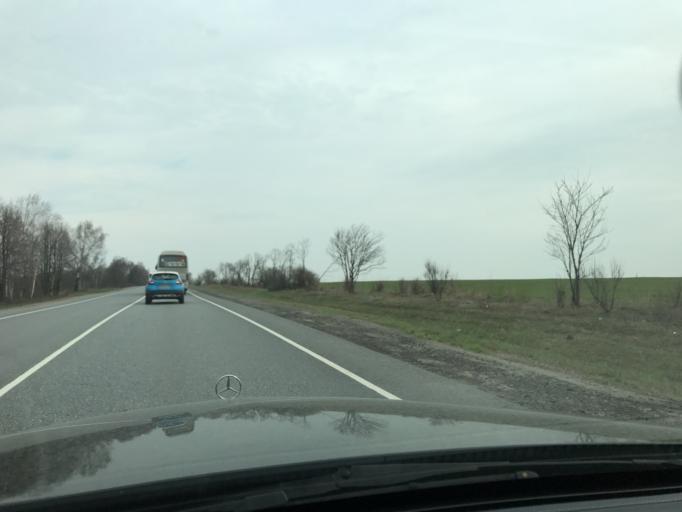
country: RU
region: Vladimir
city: Bogolyubovo
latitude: 56.2904
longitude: 40.4684
